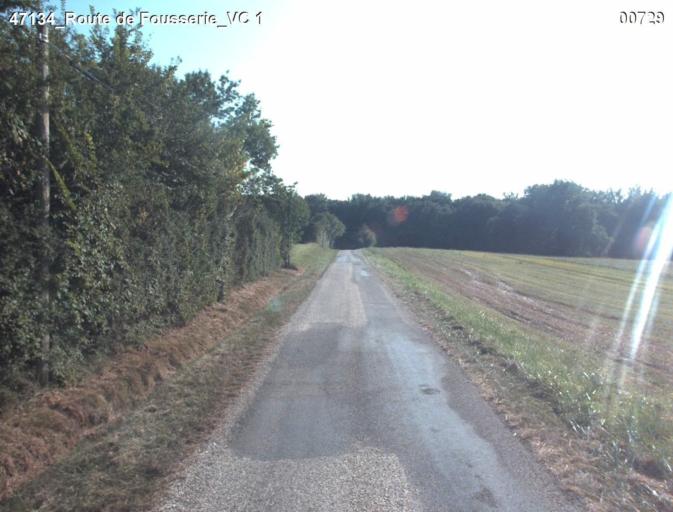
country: FR
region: Aquitaine
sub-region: Departement du Lot-et-Garonne
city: Mezin
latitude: 44.0257
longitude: 0.2780
